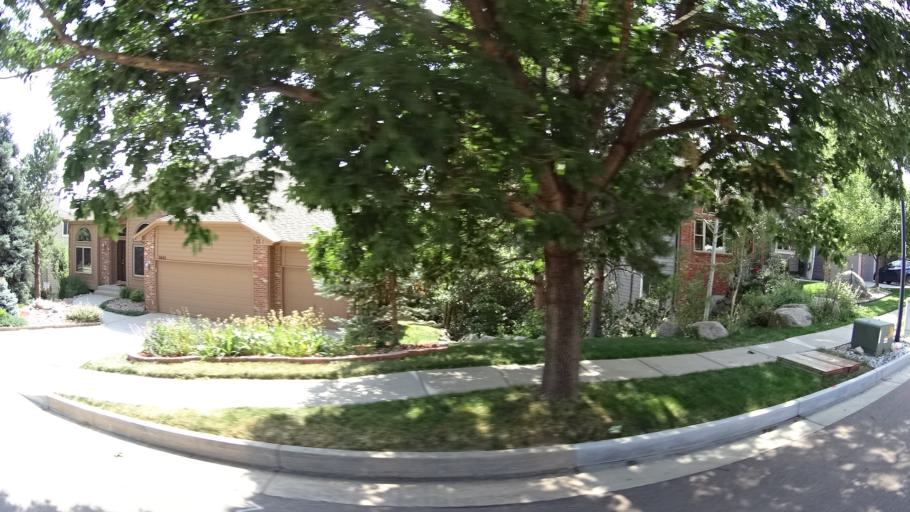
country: US
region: Colorado
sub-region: El Paso County
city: Fort Carson
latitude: 38.7485
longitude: -104.8335
